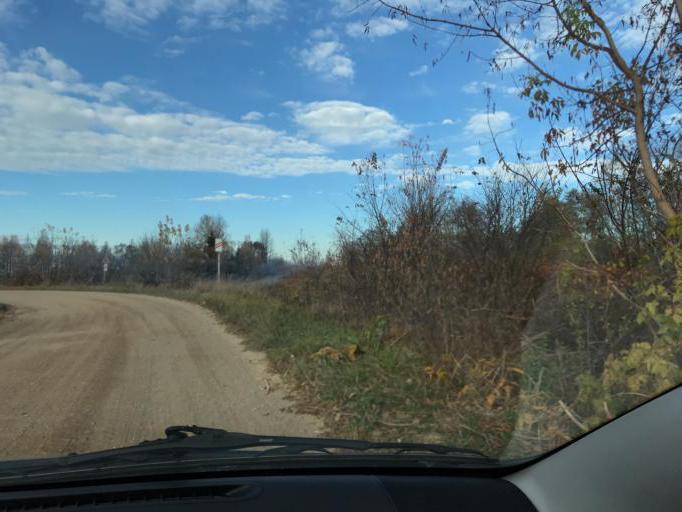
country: BY
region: Vitebsk
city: Haradok
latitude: 55.4548
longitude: 30.0202
